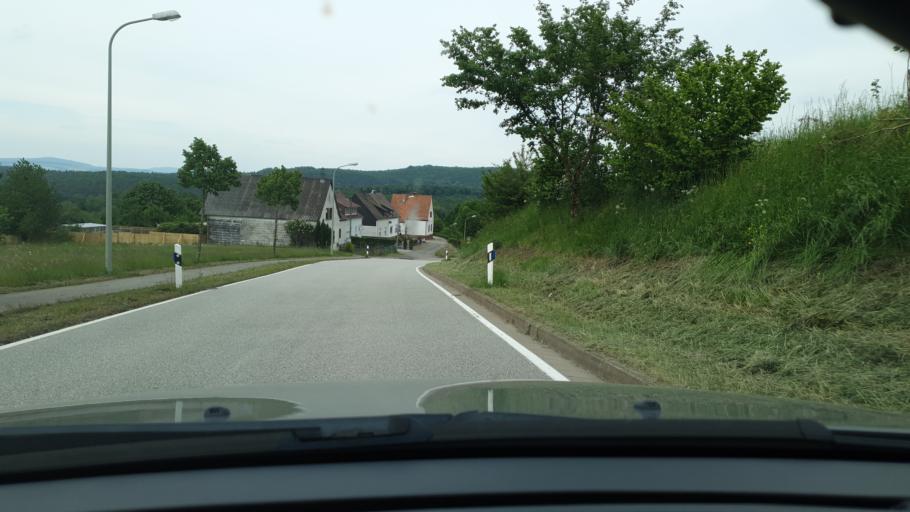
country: DE
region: Rheinland-Pfalz
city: Martinshohe
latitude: 49.3683
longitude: 7.4810
